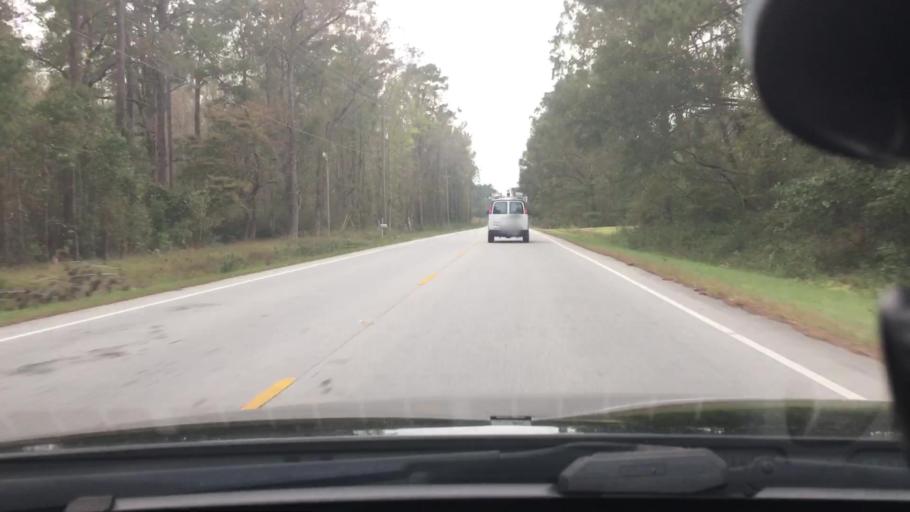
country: US
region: North Carolina
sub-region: Craven County
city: New Bern
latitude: 35.2069
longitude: -77.0596
